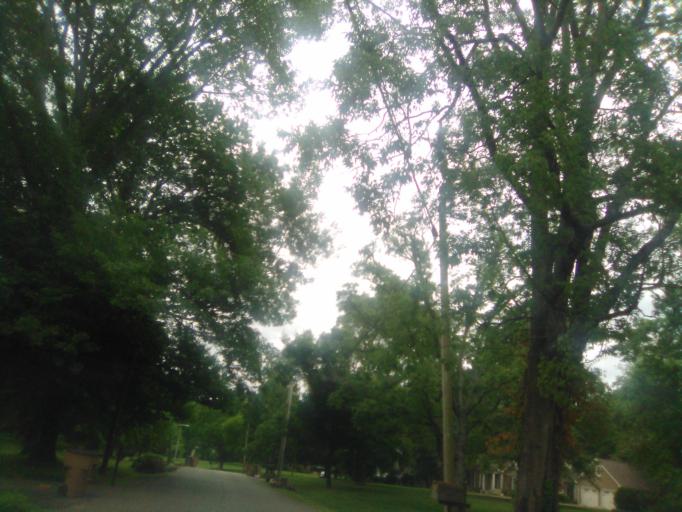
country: US
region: Tennessee
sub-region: Davidson County
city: Belle Meade
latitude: 36.1018
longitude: -86.8777
